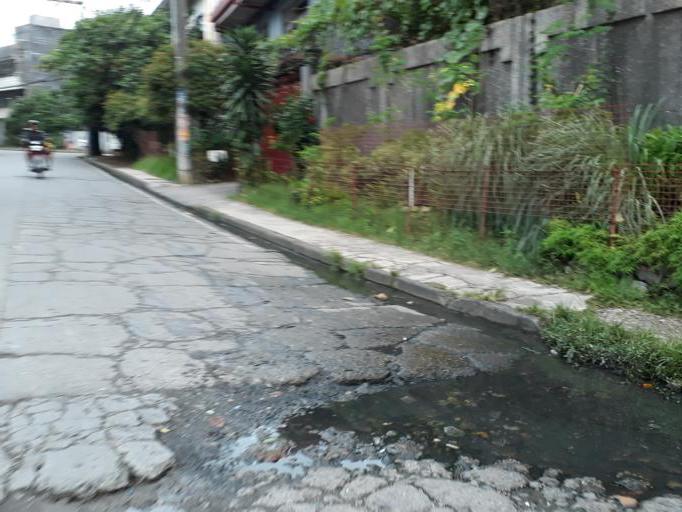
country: PH
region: Calabarzon
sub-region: Province of Rizal
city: Valenzuela
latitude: 14.6821
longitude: 120.9755
